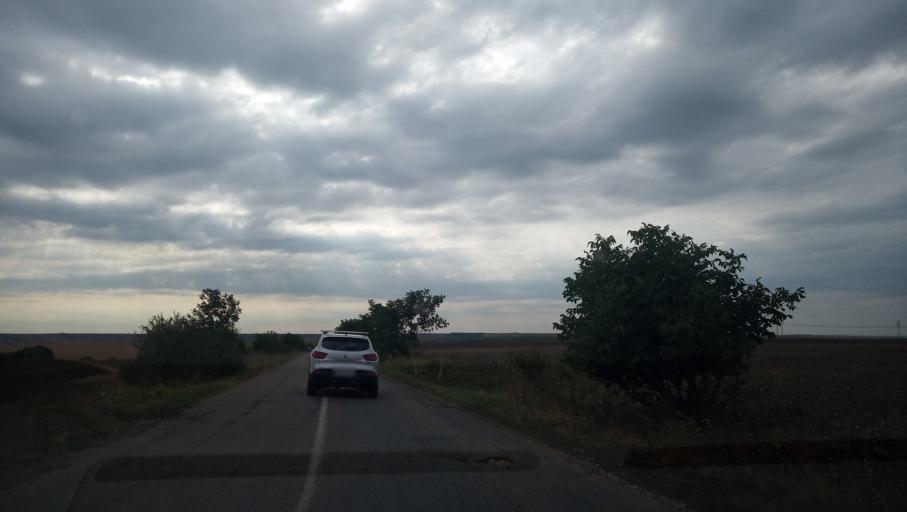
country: RO
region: Constanta
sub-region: Comuna Adamclisi
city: Adamclisi
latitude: 44.0277
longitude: 27.9901
